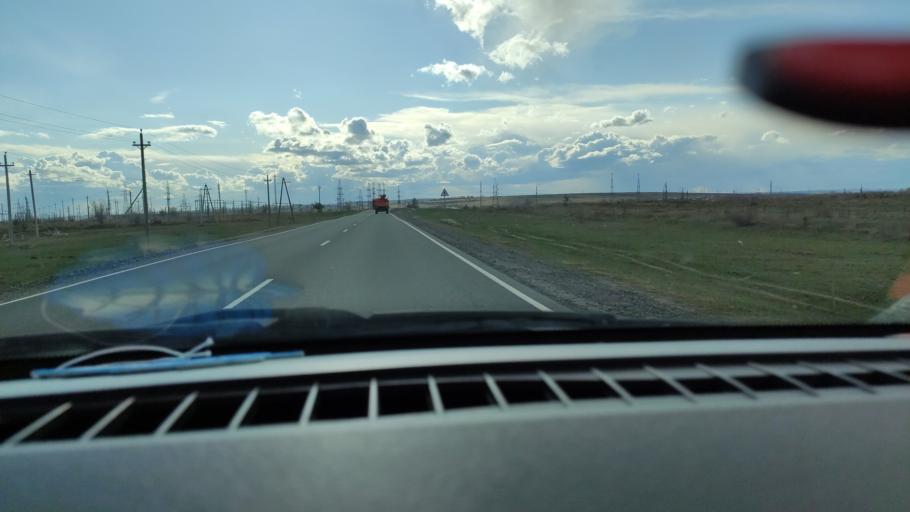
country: RU
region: Saratov
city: Sennoy
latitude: 52.1421
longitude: 46.9107
